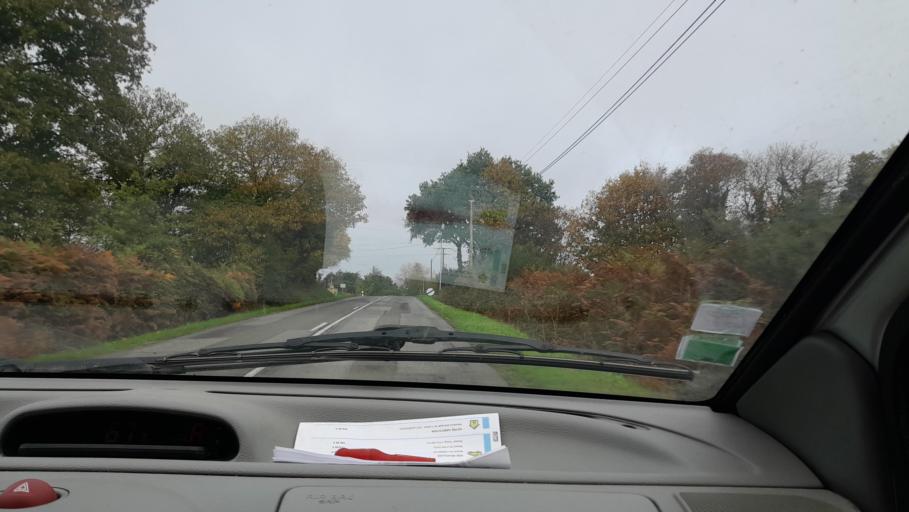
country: FR
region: Brittany
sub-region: Departement d'Ille-et-Vilaine
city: Luitre
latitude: 48.2375
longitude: -1.1103
